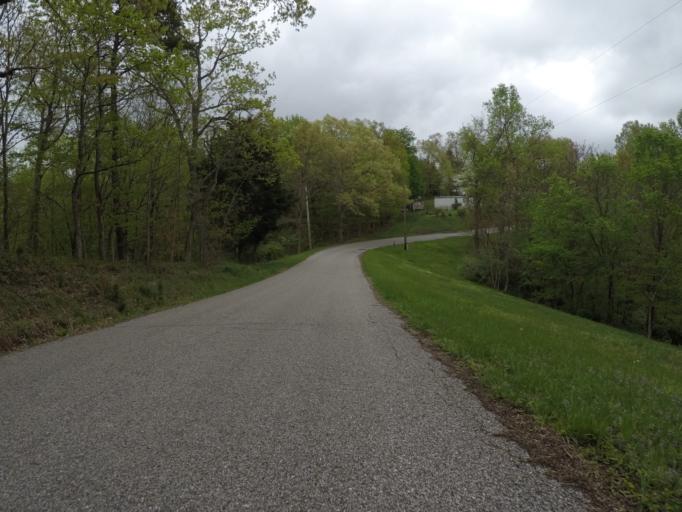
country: US
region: West Virginia
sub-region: Cabell County
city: Barboursville
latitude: 38.3974
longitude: -82.2527
